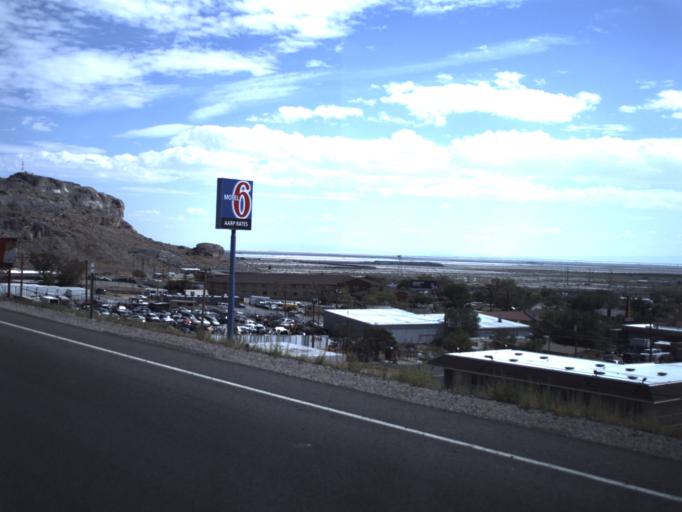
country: US
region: Utah
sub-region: Tooele County
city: Wendover
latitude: 40.7391
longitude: -114.0378
